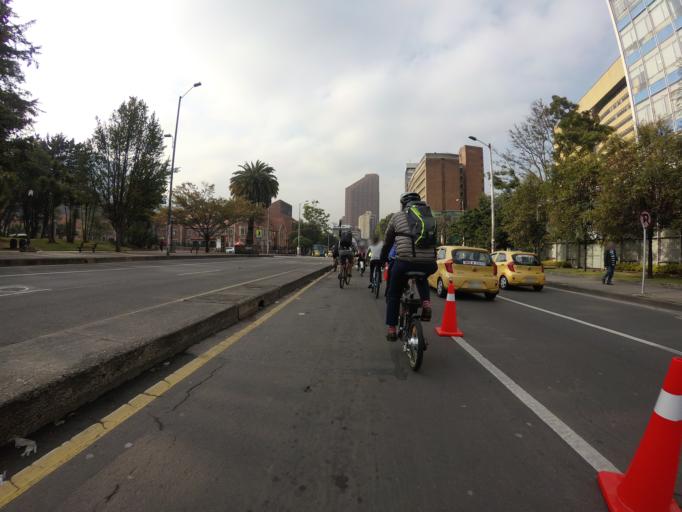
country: CO
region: Bogota D.C.
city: Bogota
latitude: 4.6238
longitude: -74.0663
